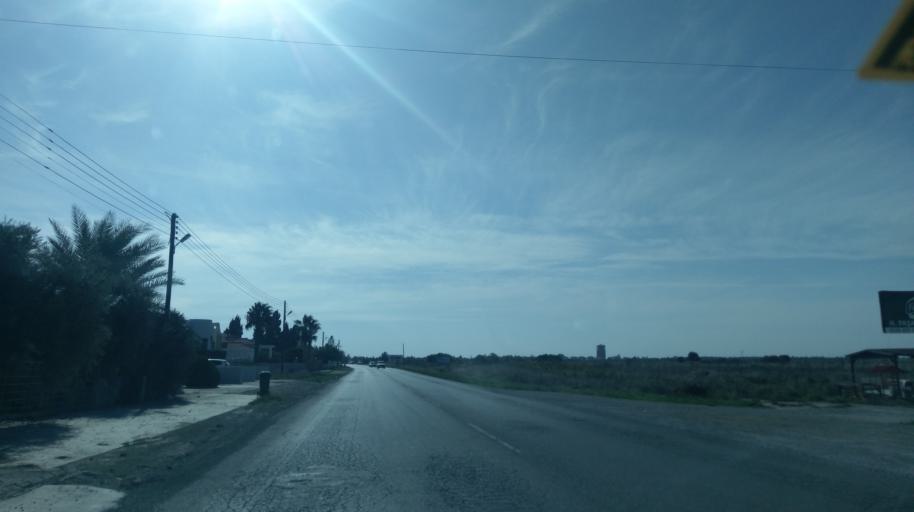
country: CY
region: Ammochostos
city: Trikomo
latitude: 35.2991
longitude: 33.9375
